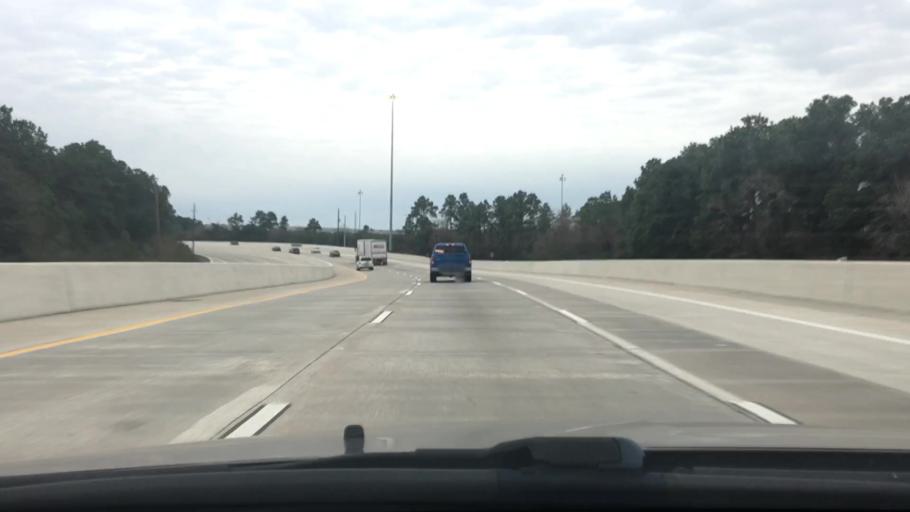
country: US
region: Texas
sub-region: Harris County
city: Spring
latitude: 30.0732
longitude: -95.4118
